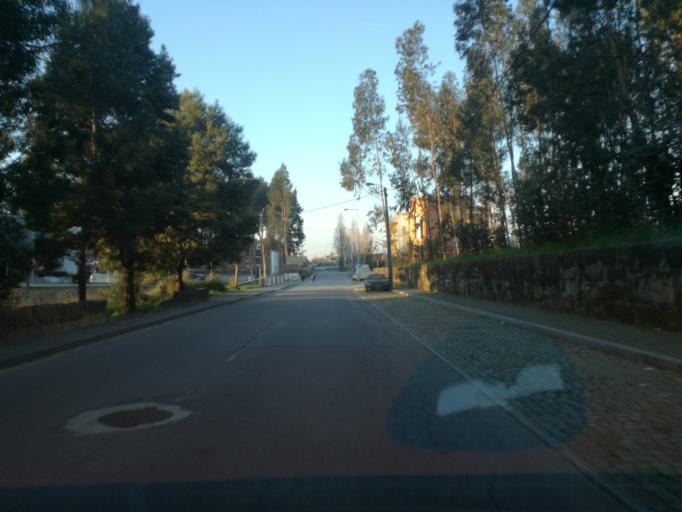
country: PT
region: Porto
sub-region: Maia
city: Milheiros
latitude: 41.2230
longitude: -8.5898
